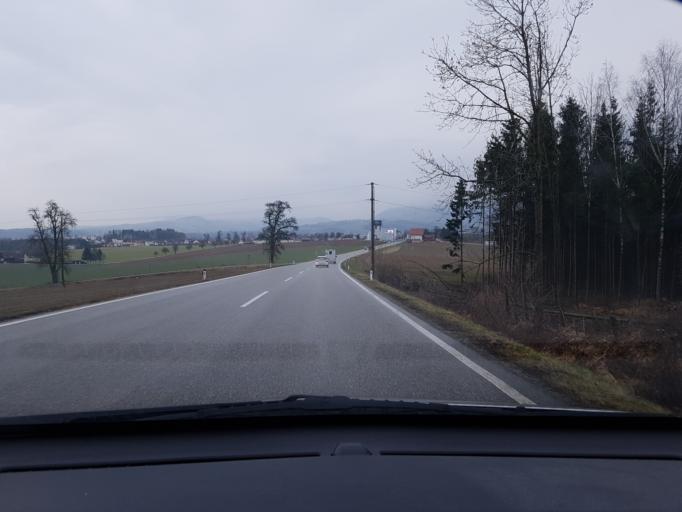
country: AT
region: Upper Austria
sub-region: Steyr Stadt
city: Steyr
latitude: 48.0555
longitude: 14.3904
